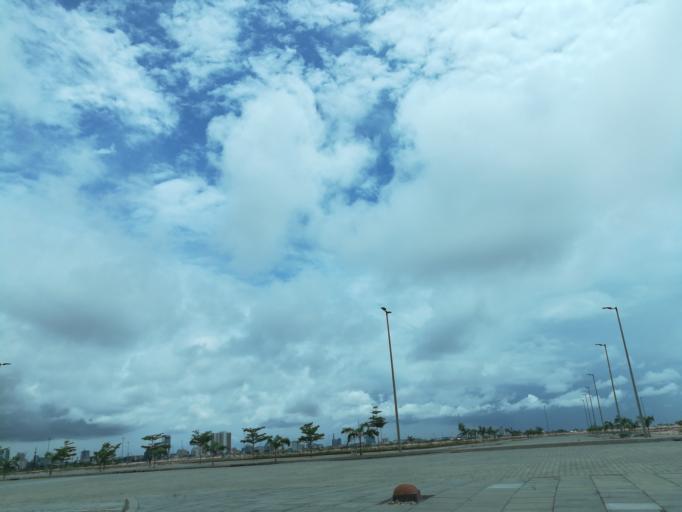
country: NG
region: Lagos
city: Ikoyi
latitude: 6.4075
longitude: 3.4184
